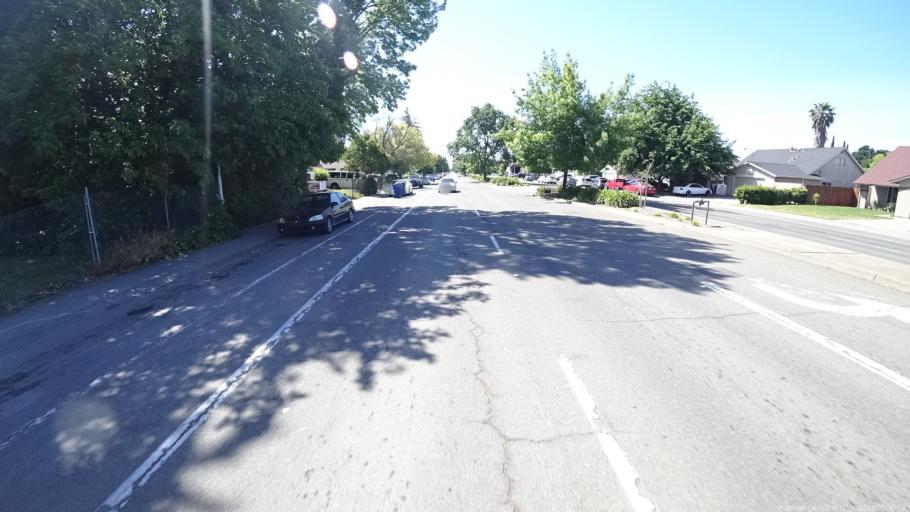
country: US
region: California
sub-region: Sacramento County
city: Florin
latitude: 38.4671
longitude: -121.4330
